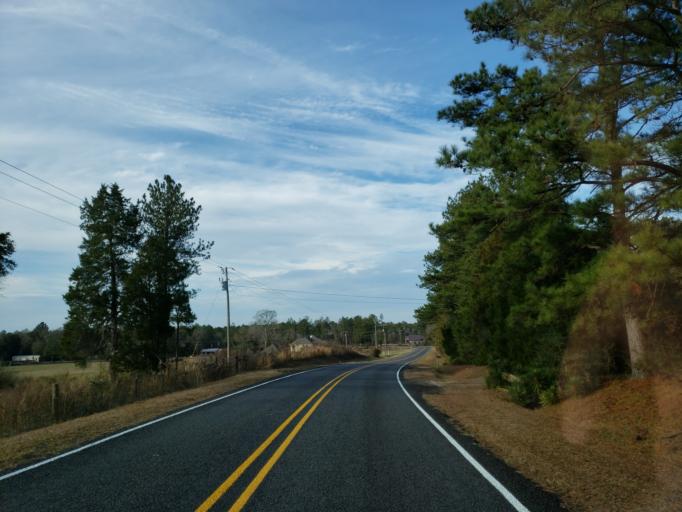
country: US
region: Mississippi
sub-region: Wayne County
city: Belmont
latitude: 31.4987
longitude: -88.5066
